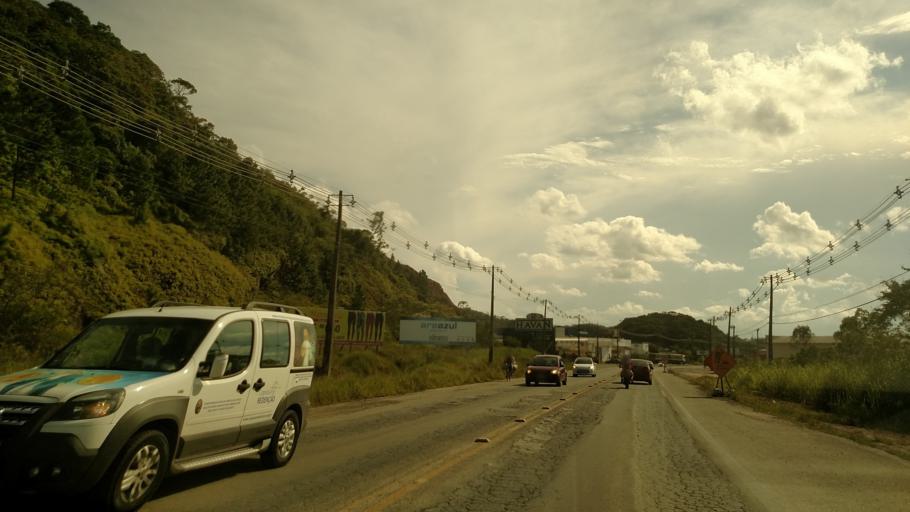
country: BR
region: Santa Catarina
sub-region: Itajai
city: Itajai
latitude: -26.9450
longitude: -48.7175
